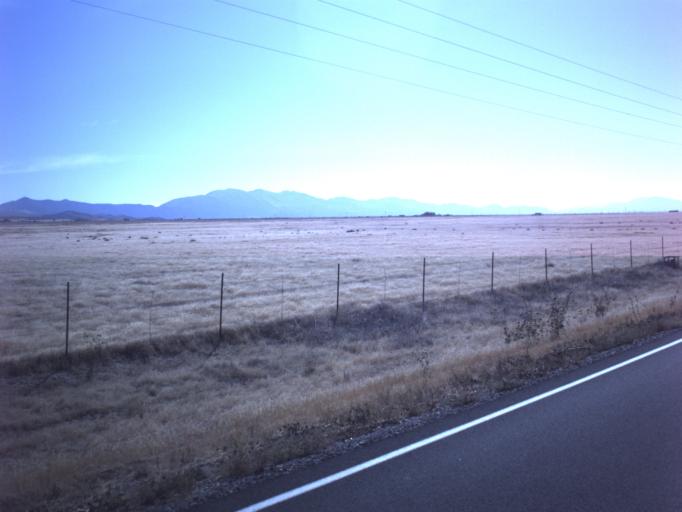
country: US
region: Utah
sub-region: Tooele County
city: Grantsville
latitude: 40.4109
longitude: -112.7484
